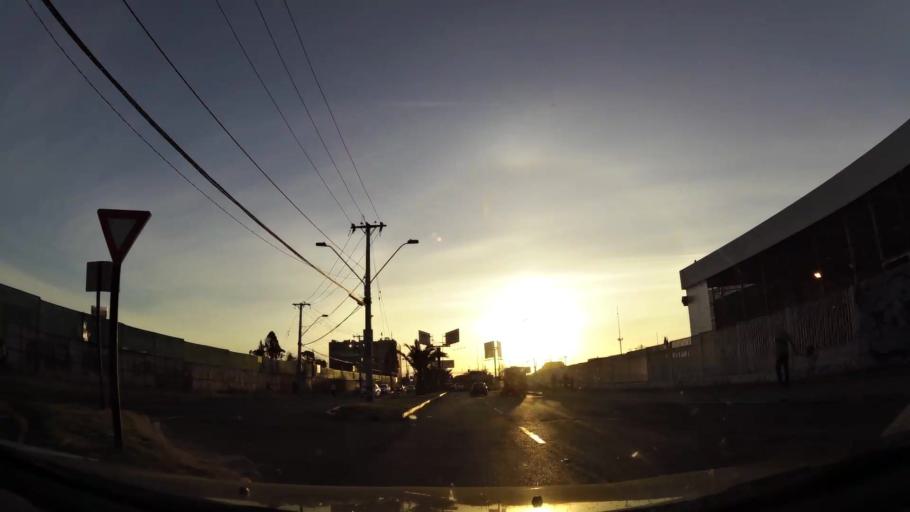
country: CL
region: Santiago Metropolitan
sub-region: Provincia de Cordillera
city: Puente Alto
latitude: -33.5980
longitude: -70.5777
